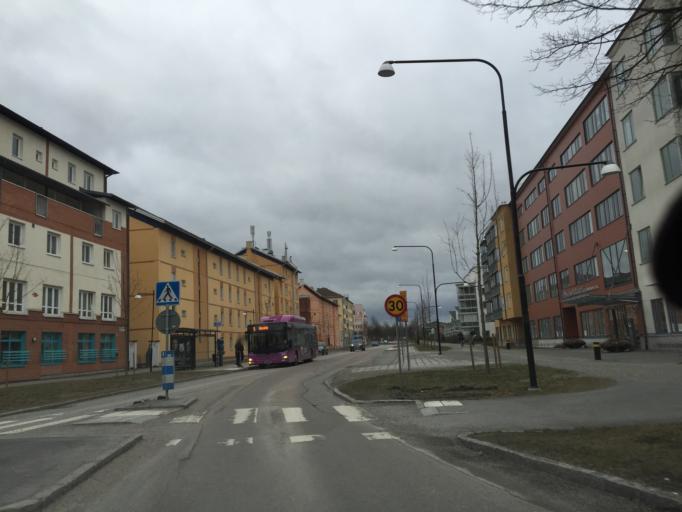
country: SE
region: OErebro
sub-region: Orebro Kommun
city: Orebro
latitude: 59.2568
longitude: 15.2056
